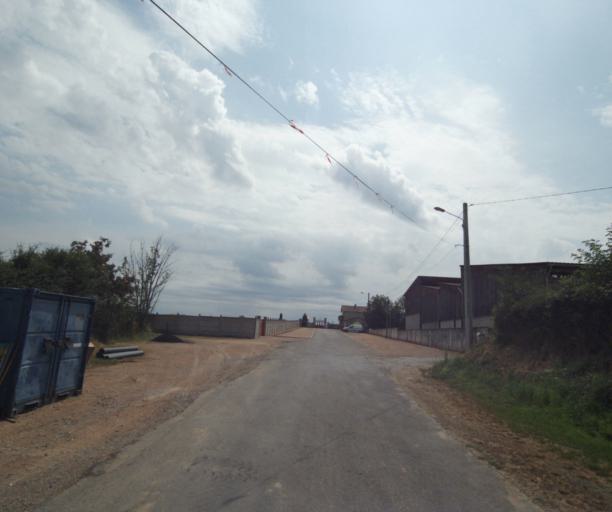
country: FR
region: Bourgogne
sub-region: Departement de Saone-et-Loire
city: Gueugnon
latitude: 46.5967
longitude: 4.0483
